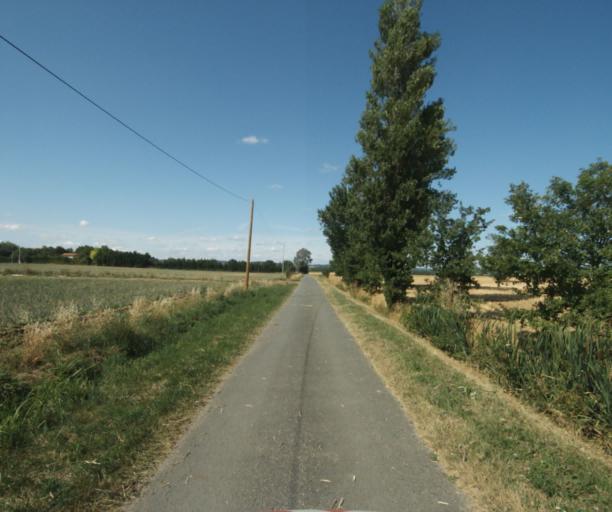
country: FR
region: Midi-Pyrenees
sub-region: Departement de la Haute-Garonne
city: Revel
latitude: 43.5038
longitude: 1.9685
